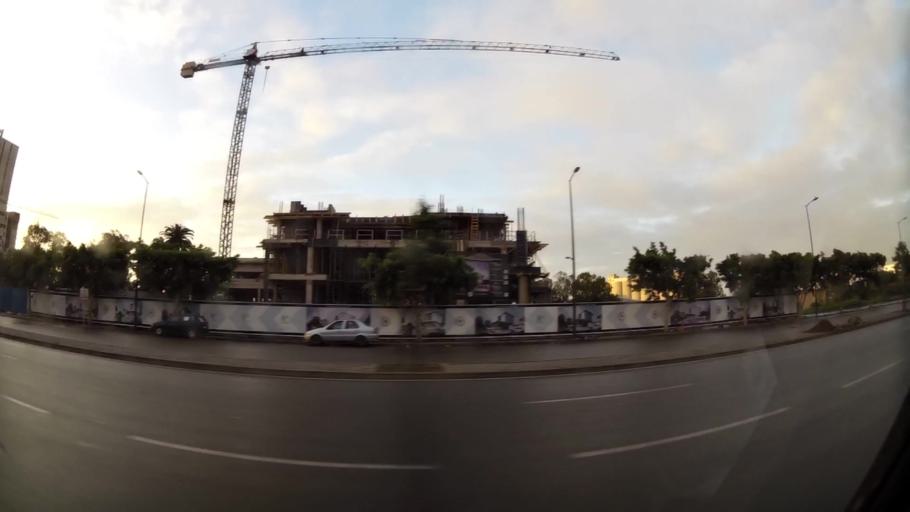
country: MA
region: Grand Casablanca
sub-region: Casablanca
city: Casablanca
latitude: 33.5961
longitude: -7.6016
